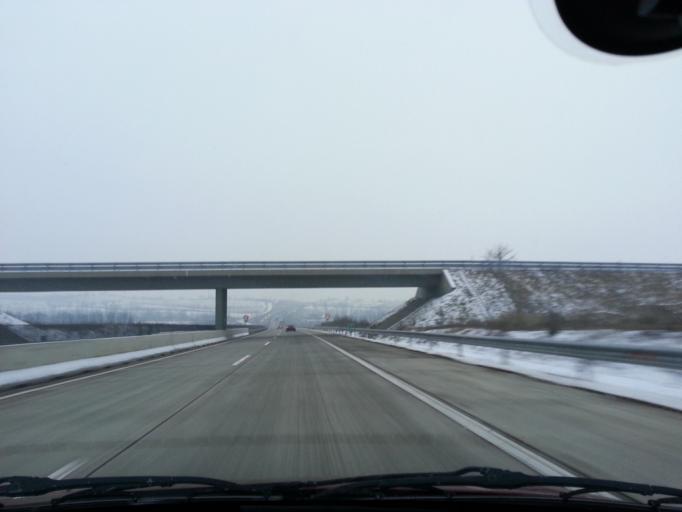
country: HU
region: Pest
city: Nagytarcsa
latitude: 47.5321
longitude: 19.3044
